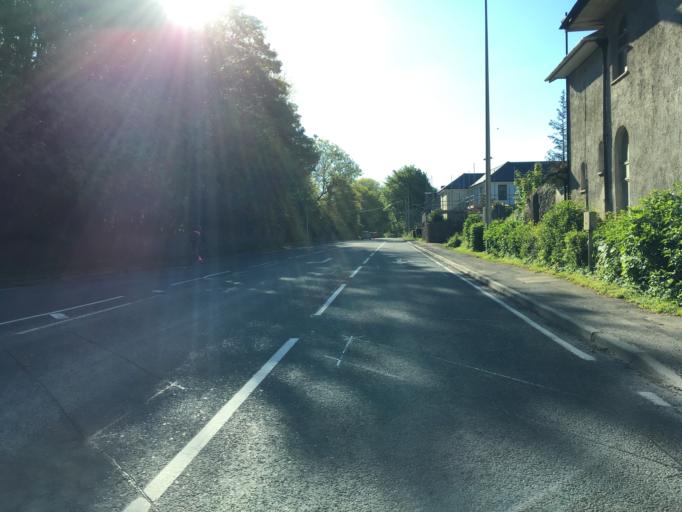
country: GB
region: England
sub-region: North Somerset
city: Long Ashton
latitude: 51.4405
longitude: -2.6848
